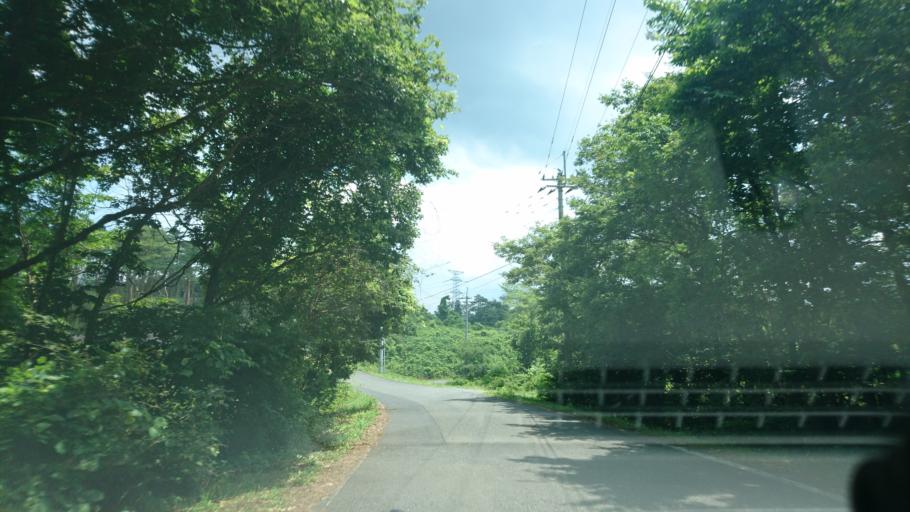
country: JP
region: Iwate
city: Ichinoseki
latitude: 38.9121
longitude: 141.2108
